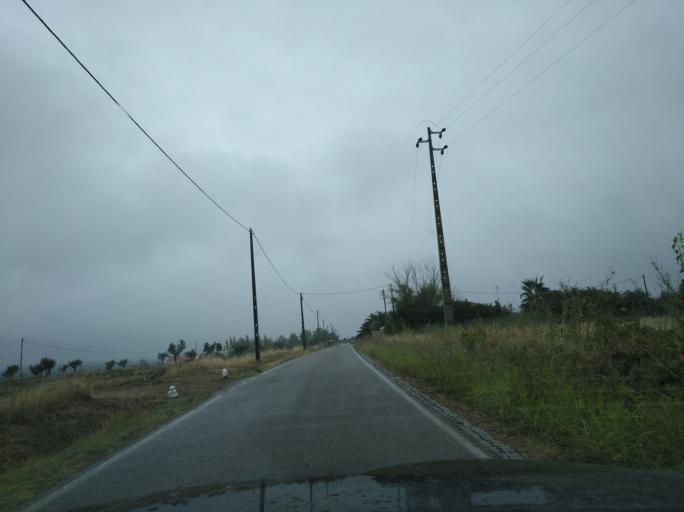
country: PT
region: Portalegre
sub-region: Campo Maior
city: Campo Maior
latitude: 38.9567
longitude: -7.0828
